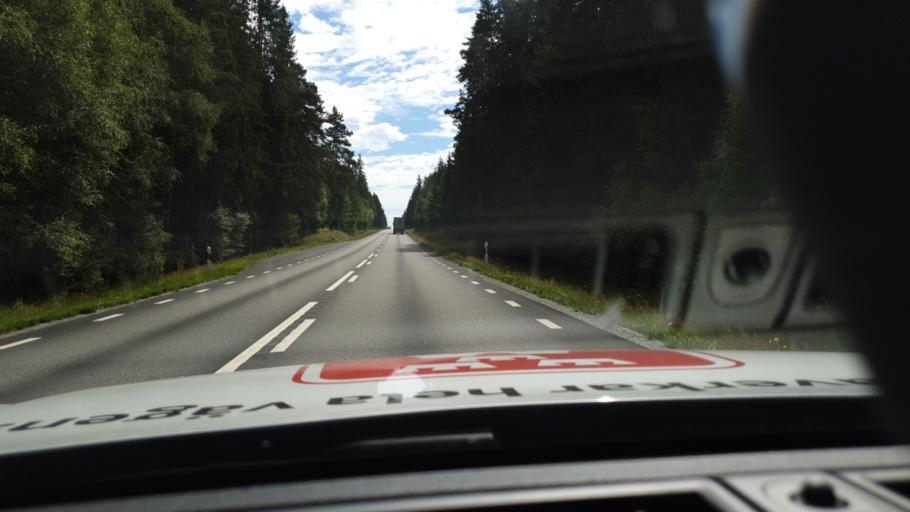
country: SE
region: Joenkoeping
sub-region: Savsjo Kommun
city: Vrigstad
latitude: 57.3280
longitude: 14.4738
